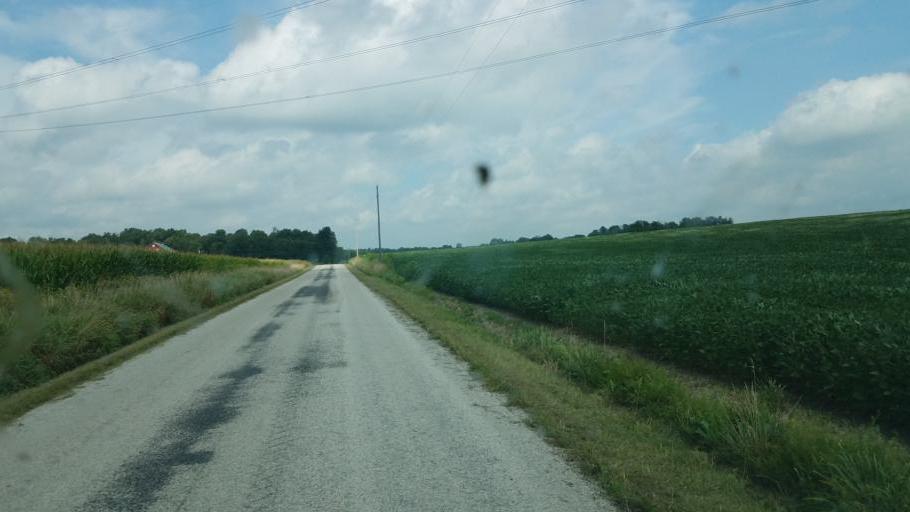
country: US
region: Ohio
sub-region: Crawford County
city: Galion
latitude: 40.6325
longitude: -82.7090
